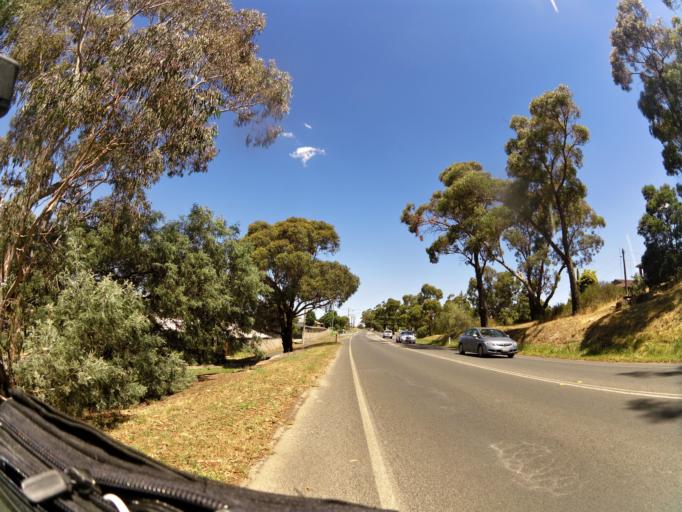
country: AU
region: Victoria
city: Mount Pleasant
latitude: -37.5951
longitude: 143.8677
